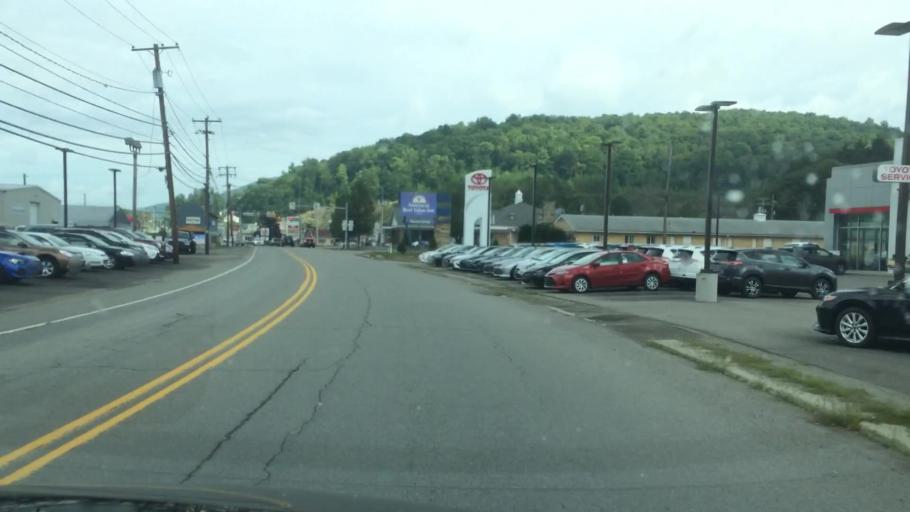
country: US
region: Pennsylvania
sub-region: McKean County
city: Foster Brook
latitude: 41.9756
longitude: -78.6172
